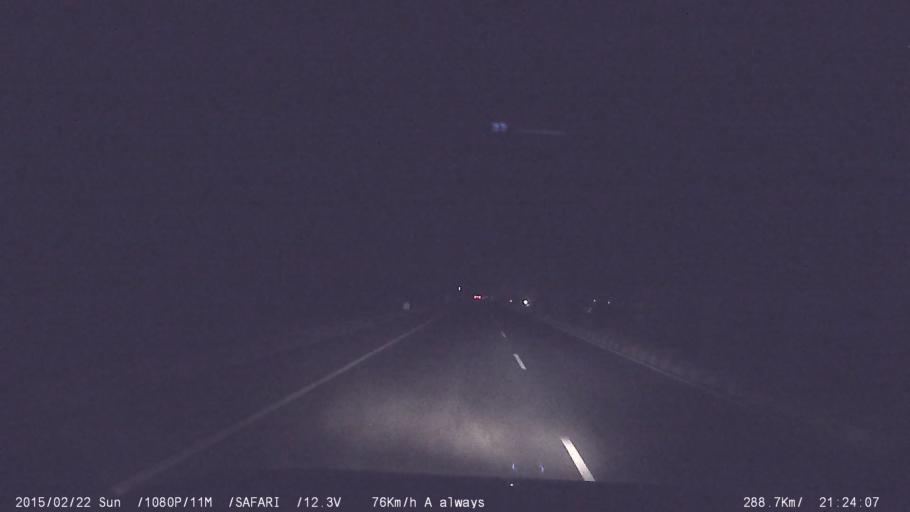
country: IN
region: Tamil Nadu
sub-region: Karur
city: Karur
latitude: 10.8859
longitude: 78.0145
